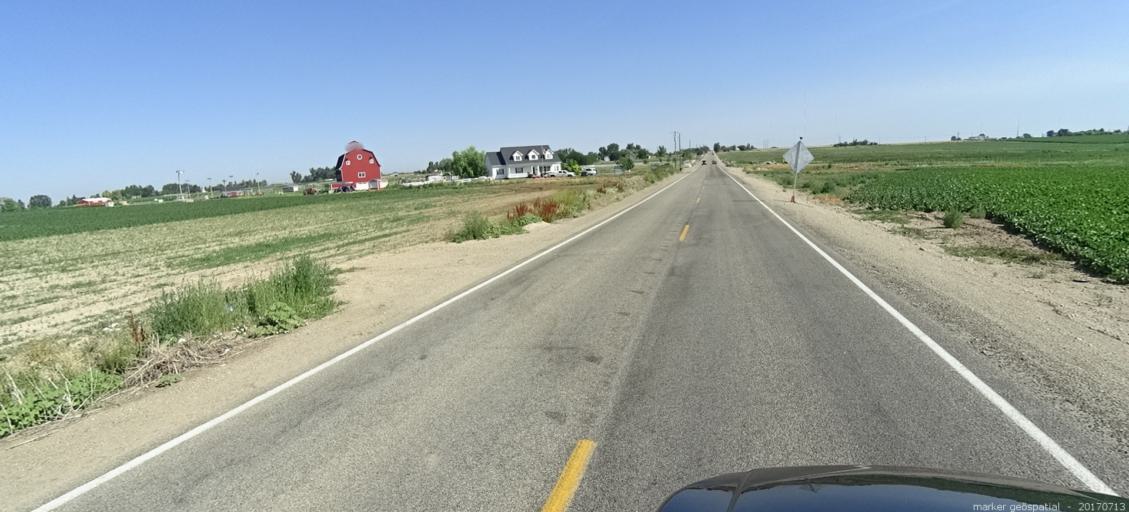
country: US
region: Idaho
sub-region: Ada County
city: Kuna
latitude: 43.5383
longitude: -116.4138
